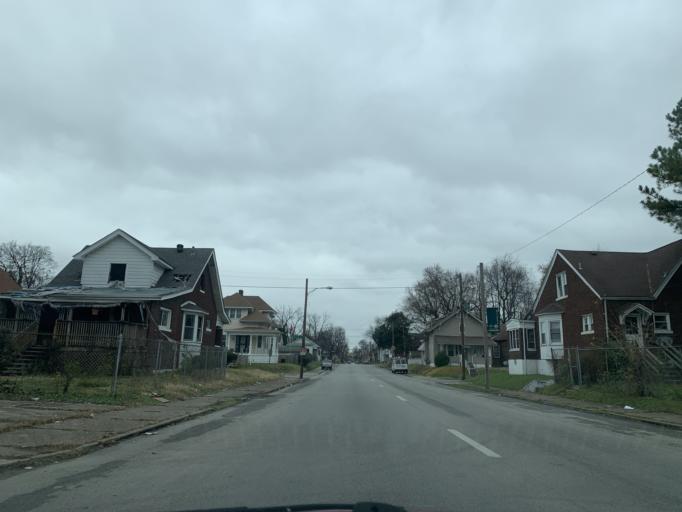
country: US
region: Kentucky
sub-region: Jefferson County
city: Louisville
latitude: 38.2387
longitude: -85.7884
